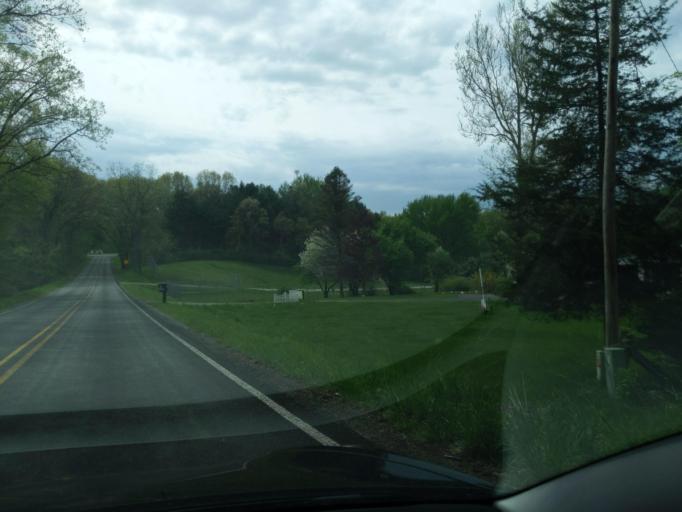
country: US
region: Michigan
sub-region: Washtenaw County
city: Chelsea
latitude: 42.3806
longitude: -84.0747
